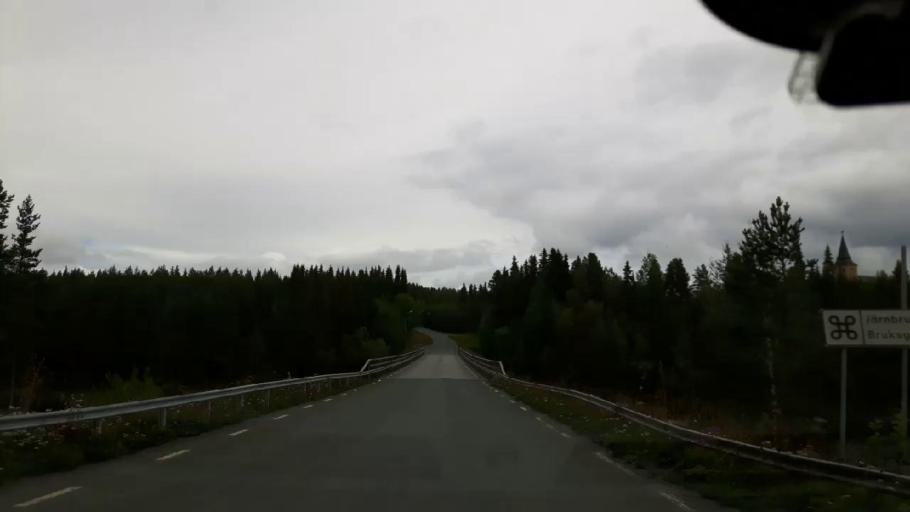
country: SE
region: Jaemtland
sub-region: Krokoms Kommun
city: Valla
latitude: 63.6456
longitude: 13.8288
